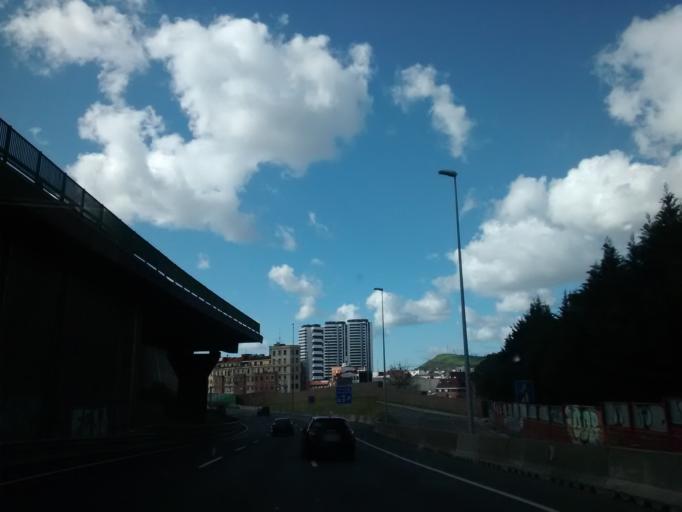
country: ES
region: Basque Country
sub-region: Bizkaia
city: Bilbao
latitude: 43.2540
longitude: -2.9486
